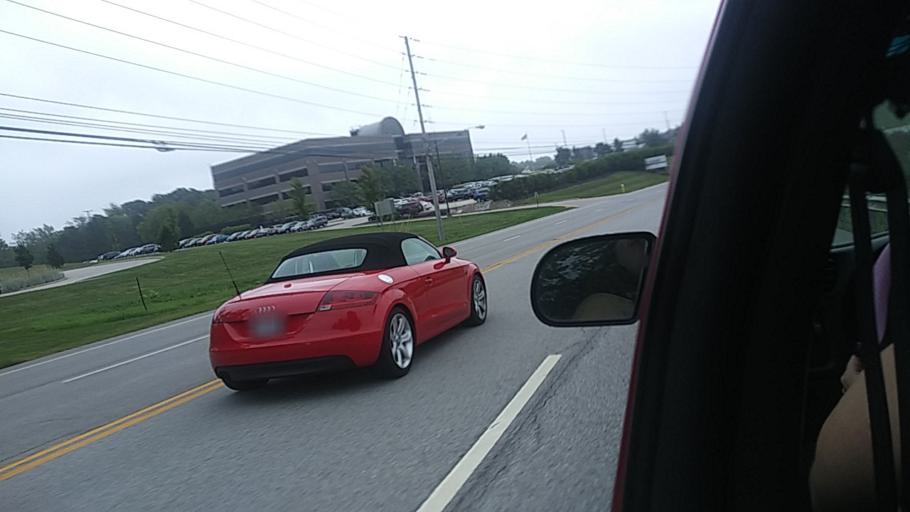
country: US
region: Ohio
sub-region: Summit County
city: Fairlawn
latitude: 41.1419
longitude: -81.6167
